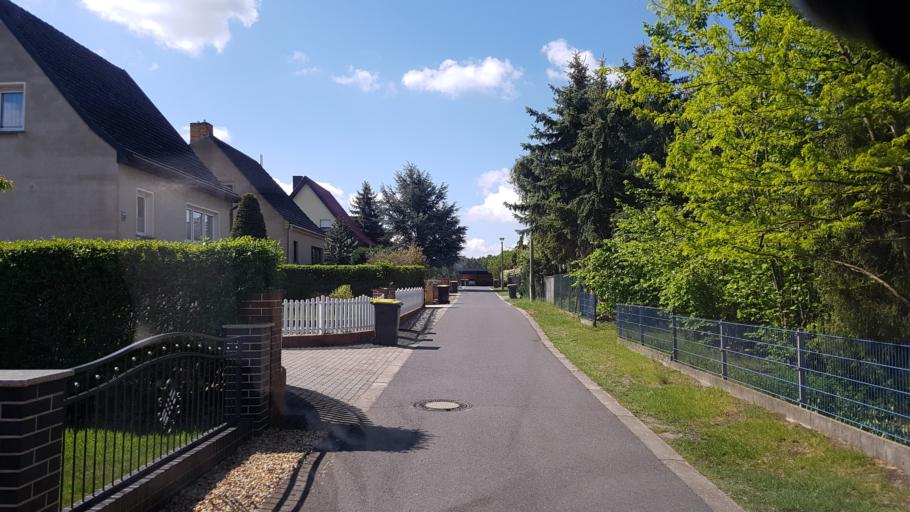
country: DE
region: Brandenburg
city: Bronkow
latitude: 51.5914
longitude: 13.9248
